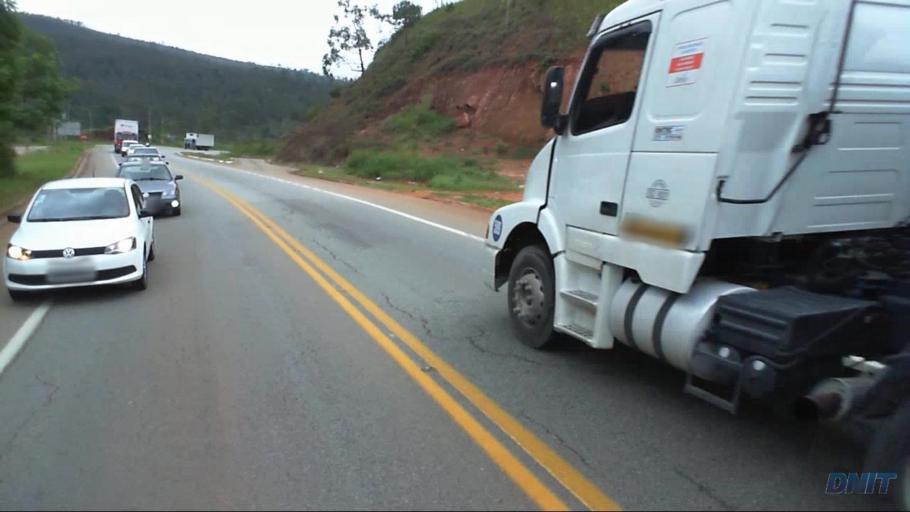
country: BR
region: Minas Gerais
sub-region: Joao Monlevade
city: Joao Monlevade
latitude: -19.8274
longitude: -43.0862
